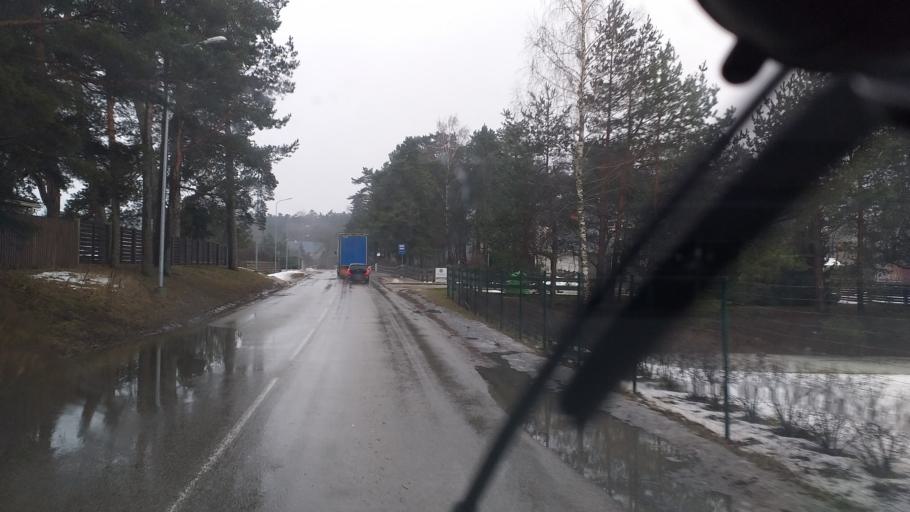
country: LV
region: Babite
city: Pinki
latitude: 56.9769
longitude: 23.9700
